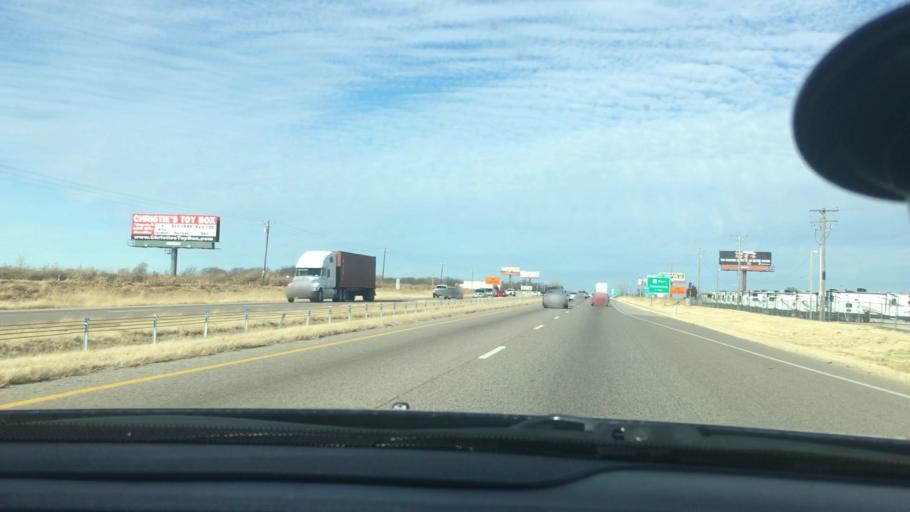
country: US
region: Oklahoma
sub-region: McClain County
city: Goldsby
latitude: 35.1572
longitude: -97.4804
